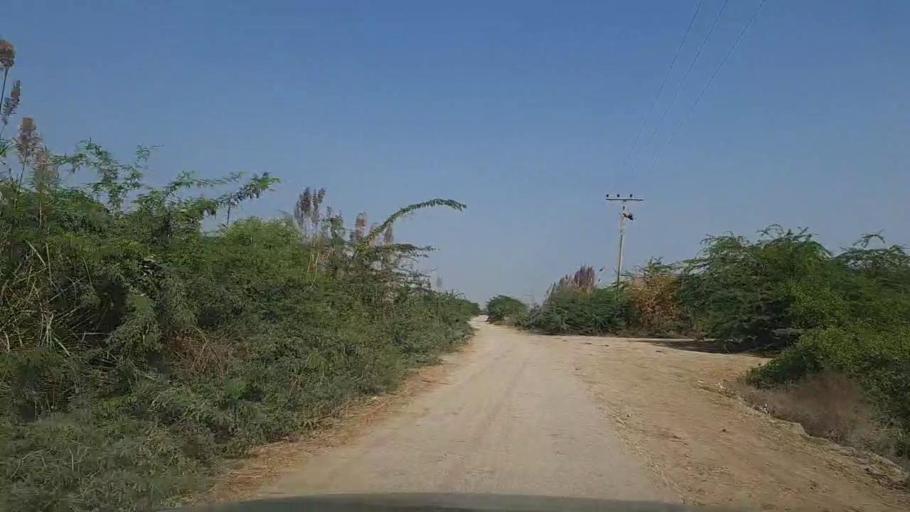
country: PK
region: Sindh
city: Thatta
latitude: 24.5945
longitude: 67.9496
